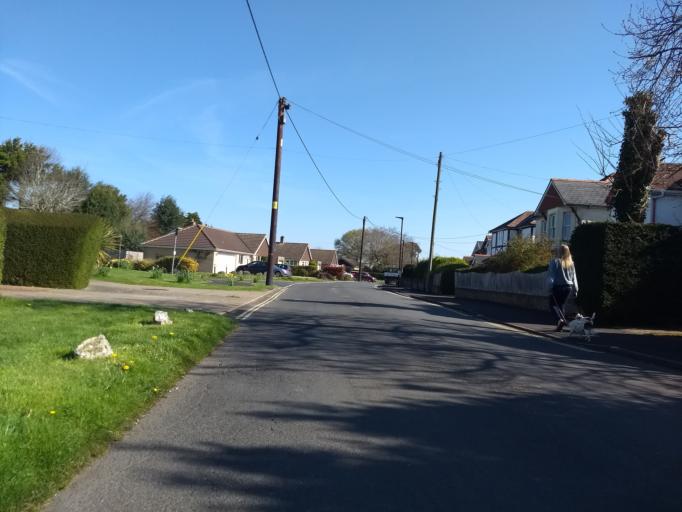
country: GB
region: England
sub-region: Isle of Wight
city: East Cowes
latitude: 50.7277
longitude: -1.2402
